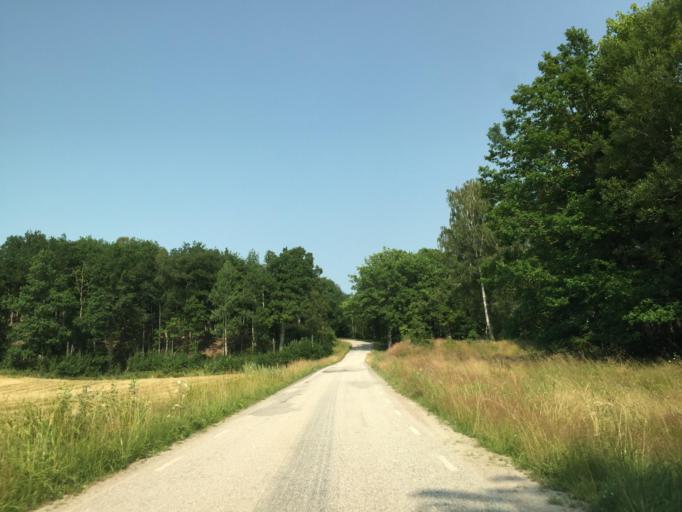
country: SE
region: Vaestra Goetaland
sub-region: Trollhattan
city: Sjuntorp
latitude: 58.2760
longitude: 12.1151
